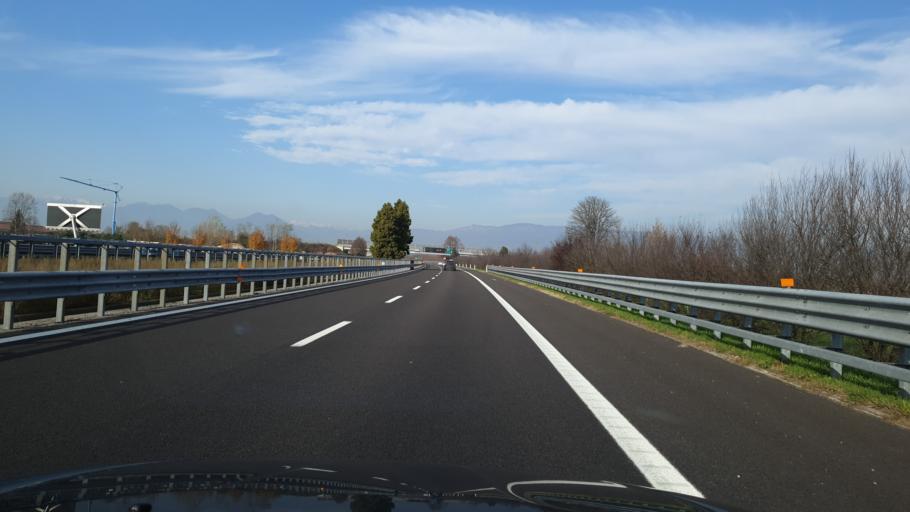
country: IT
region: Veneto
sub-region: Provincia di Vicenza
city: Vigardolo
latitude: 45.6226
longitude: 11.5952
